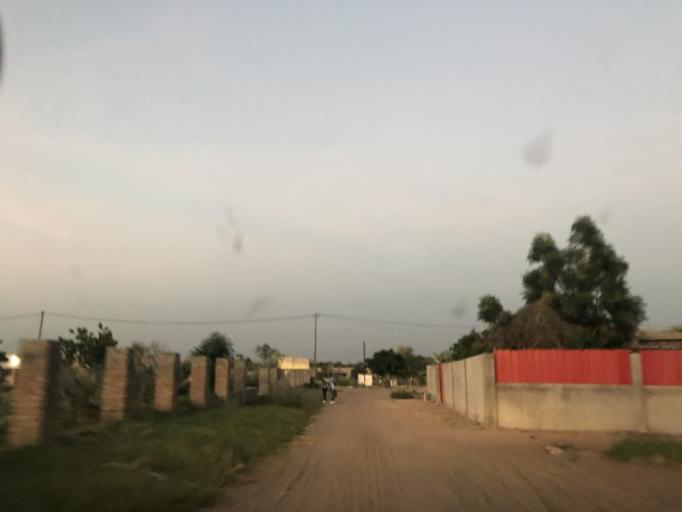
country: AO
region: Cunene
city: Ondjiva
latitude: -17.0624
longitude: 15.7058
